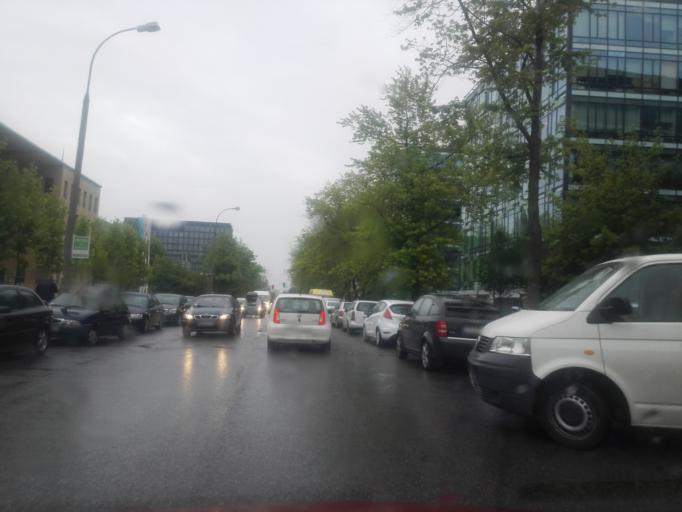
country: PL
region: Masovian Voivodeship
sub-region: Warszawa
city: Ochota
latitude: 52.1831
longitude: 20.9949
